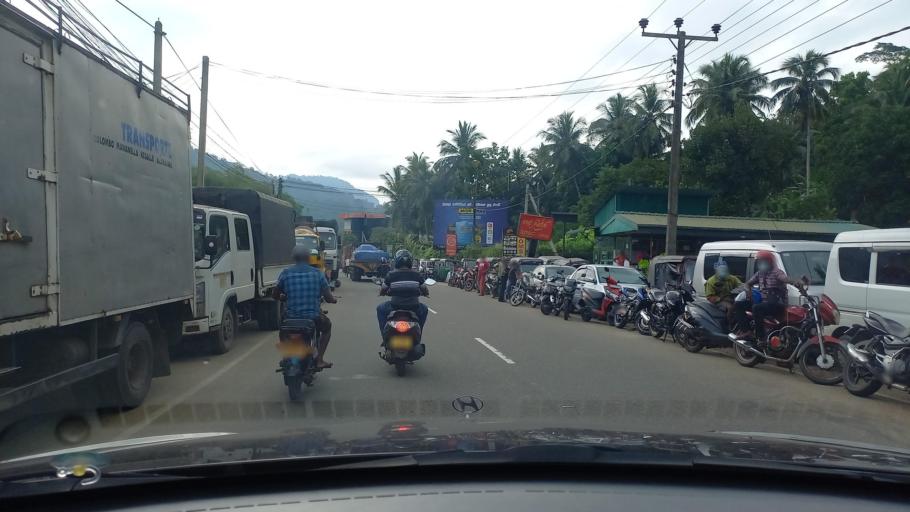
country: LK
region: Central
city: Kadugannawa
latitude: 7.2492
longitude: 80.4594
